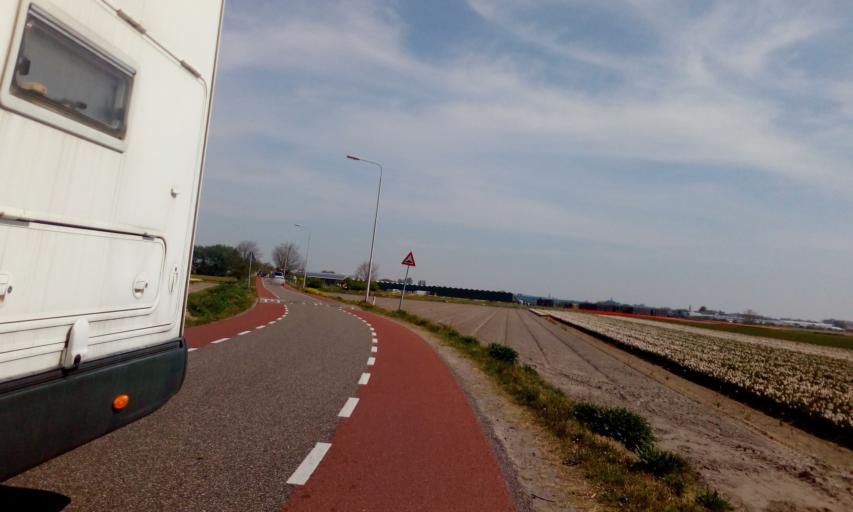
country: NL
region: South Holland
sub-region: Gemeente Lisse
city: Lisse
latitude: 52.2791
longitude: 4.5516
